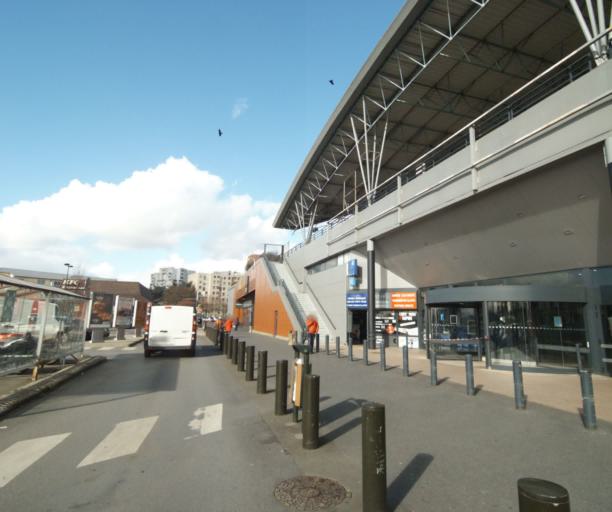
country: FR
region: Ile-de-France
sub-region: Departement de Seine-Saint-Denis
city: Villetaneuse
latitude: 48.9492
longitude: 2.3437
